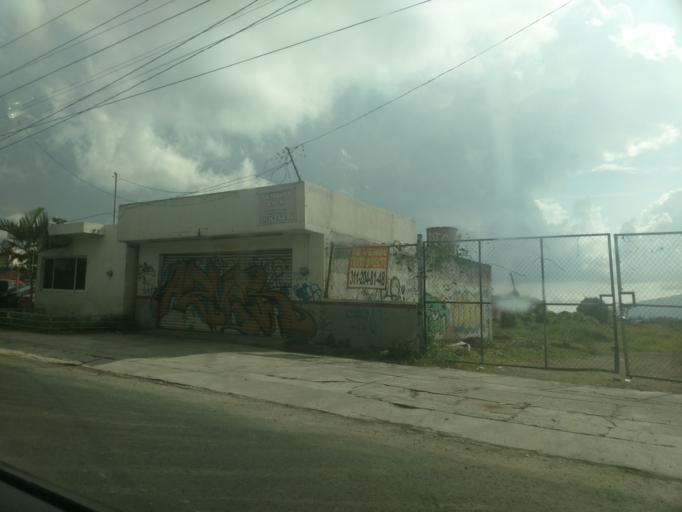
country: MX
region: Nayarit
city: Tepic
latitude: 21.4947
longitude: -104.8687
